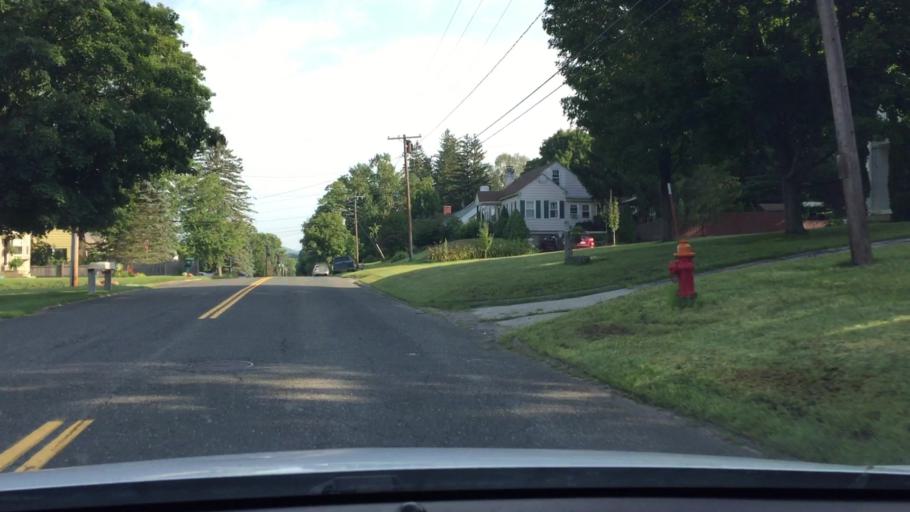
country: US
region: Massachusetts
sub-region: Berkshire County
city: Lee
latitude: 42.3118
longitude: -73.2329
